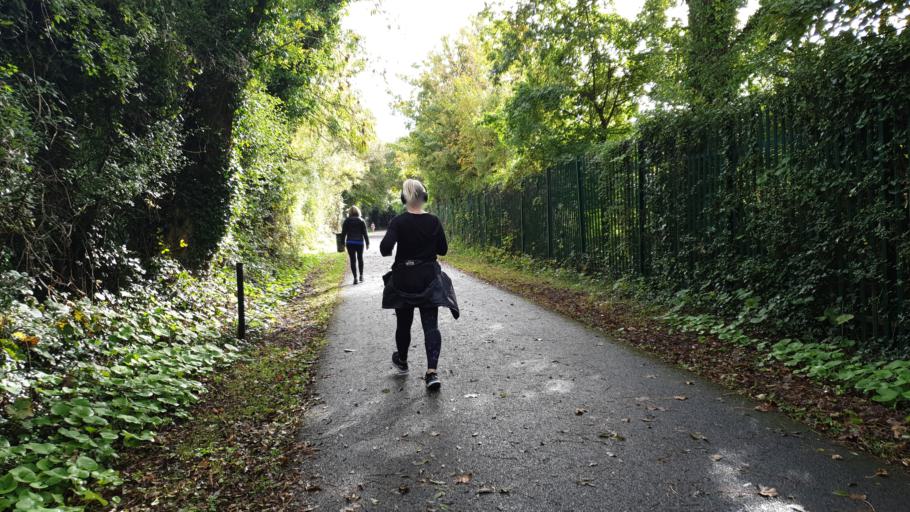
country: IE
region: Munster
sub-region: County Cork
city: Cork
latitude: 51.8994
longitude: -8.4260
